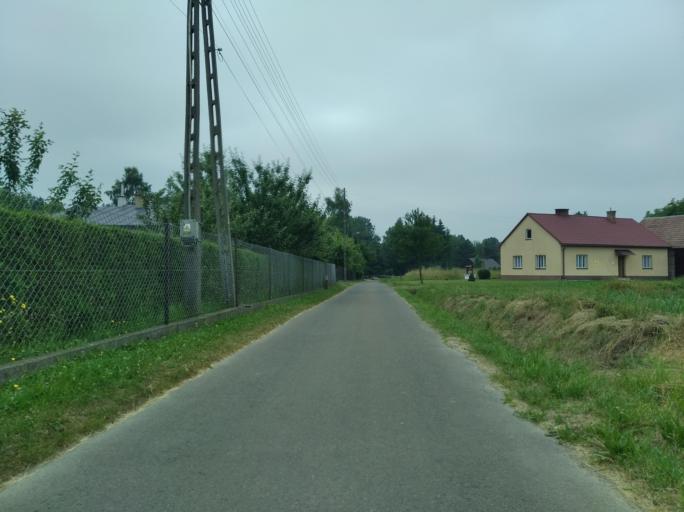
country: PL
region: Subcarpathian Voivodeship
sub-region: Powiat brzozowski
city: Jablonica Polska
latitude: 49.6963
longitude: 21.8927
